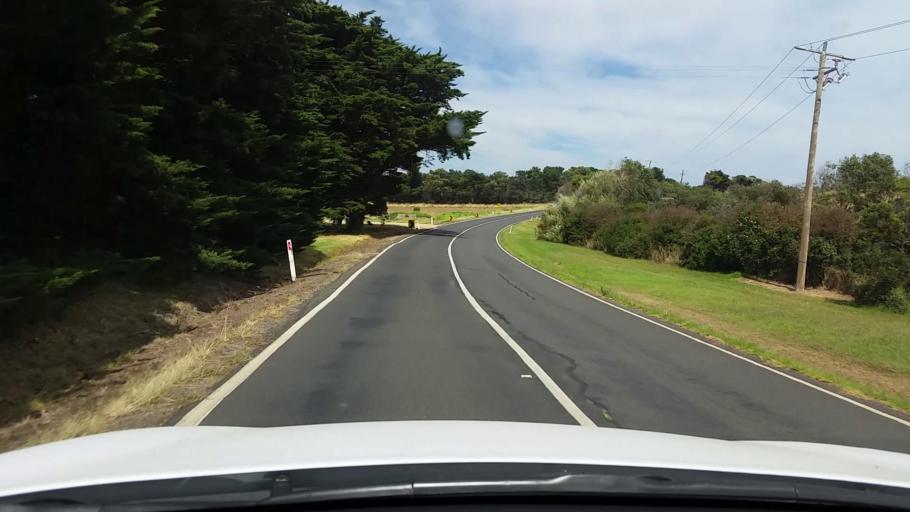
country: AU
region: Victoria
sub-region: Mornington Peninsula
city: Merricks
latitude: -38.4785
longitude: 144.9923
